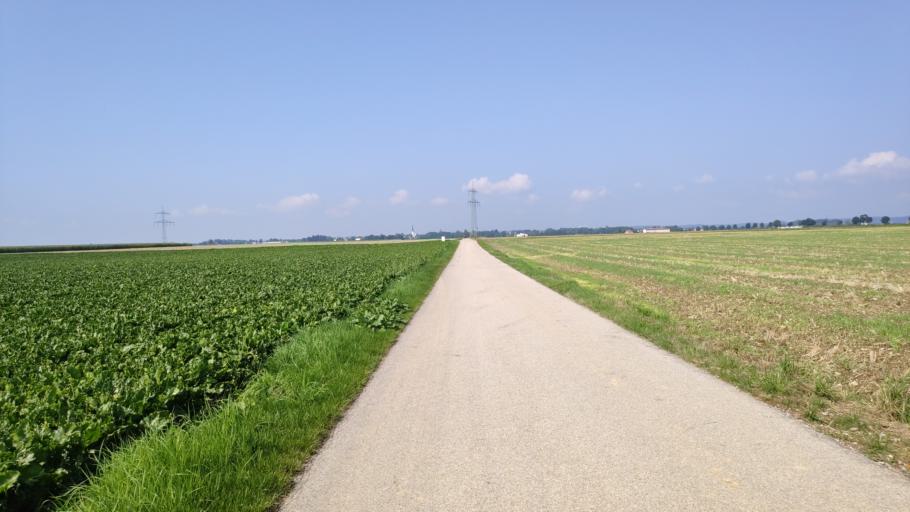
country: DE
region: Bavaria
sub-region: Swabia
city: Graben
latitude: 48.1854
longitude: 10.7986
